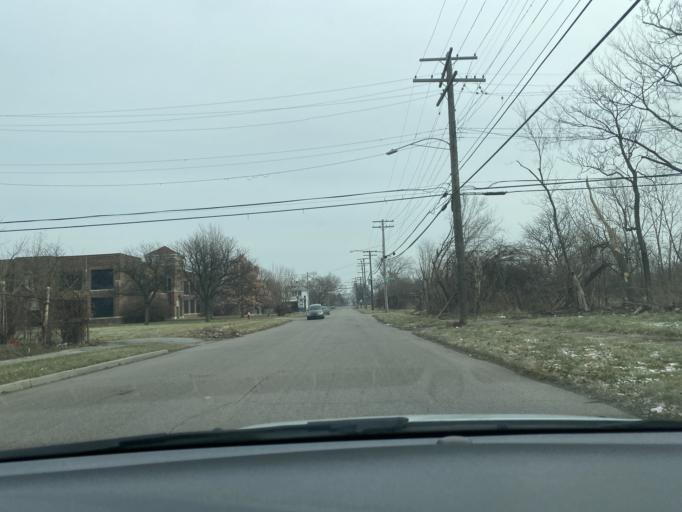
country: US
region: Michigan
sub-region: Wayne County
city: Highland Park
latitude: 42.3730
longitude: -83.1332
